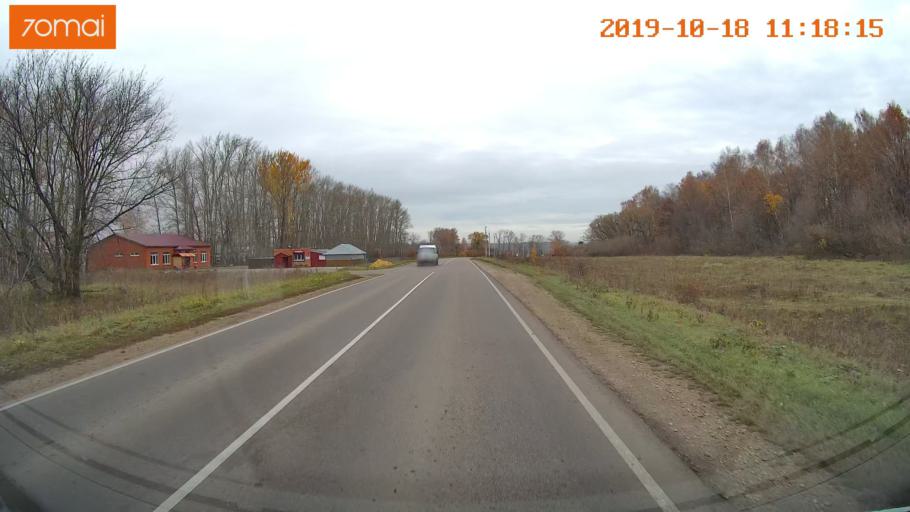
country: RU
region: Tula
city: Kimovsk
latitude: 54.0369
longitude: 38.5503
